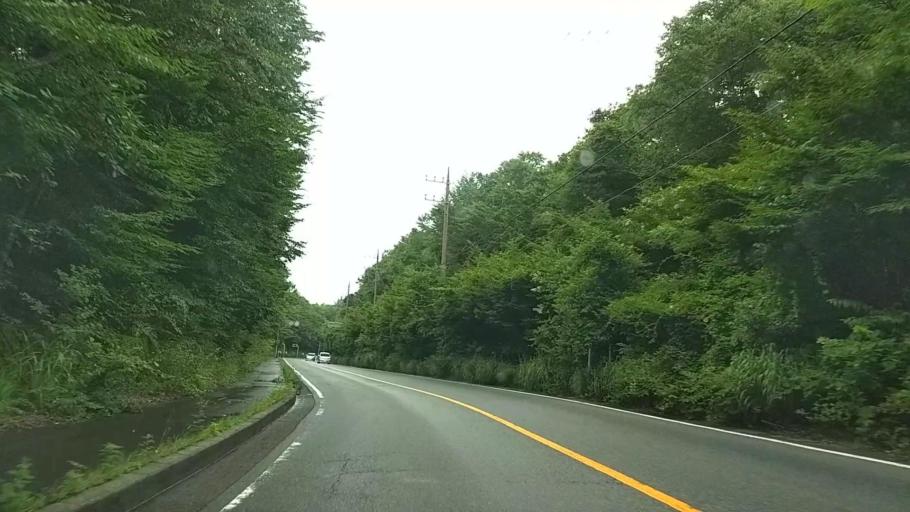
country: JP
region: Yamanashi
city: Fujikawaguchiko
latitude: 35.4863
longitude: 138.6351
